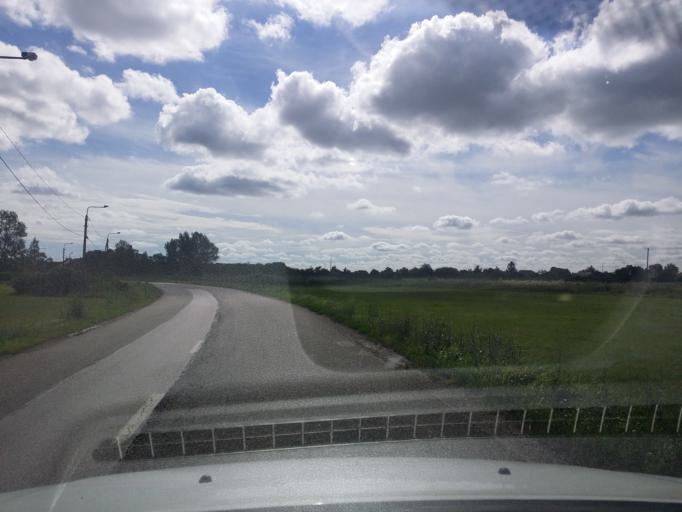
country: HU
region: Heves
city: Karacsond
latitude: 47.6855
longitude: 20.0954
